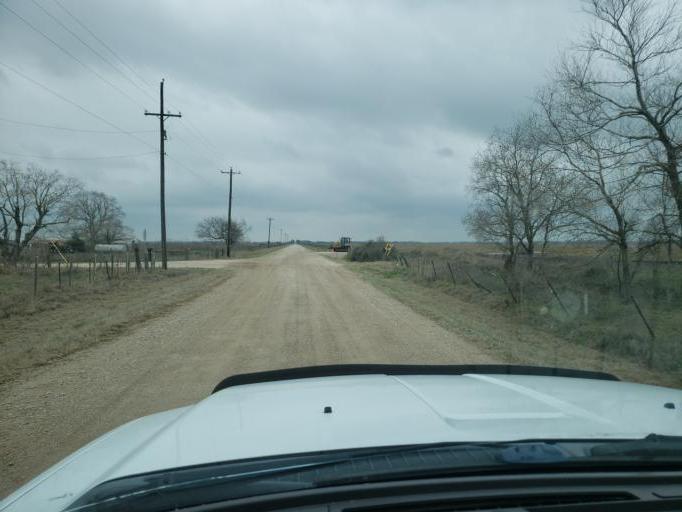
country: US
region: Texas
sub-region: Fort Bend County
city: Needville
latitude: 29.3608
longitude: -95.7345
